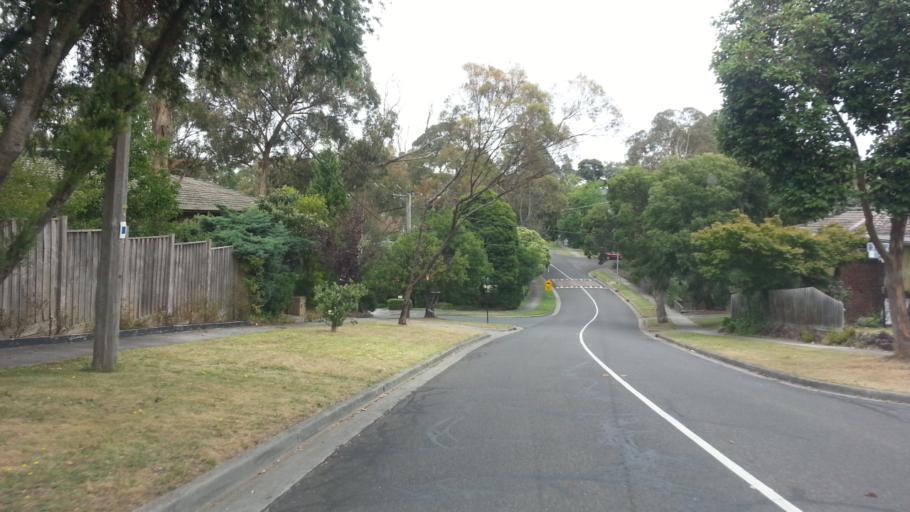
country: AU
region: Victoria
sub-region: Whitehorse
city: Vermont
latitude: -37.8312
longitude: 145.2029
